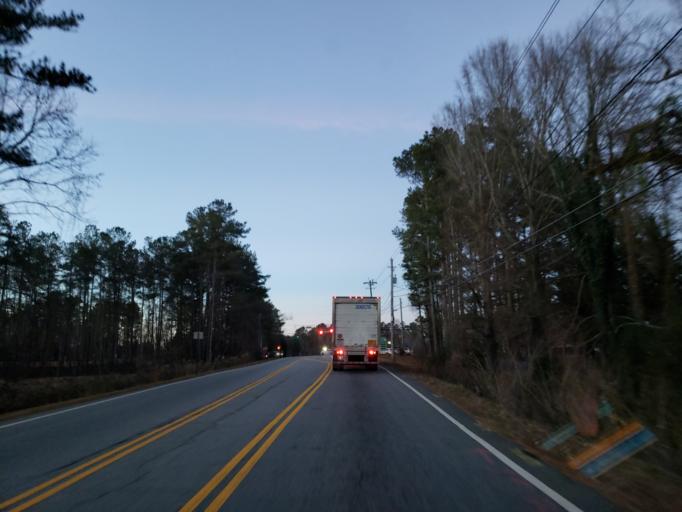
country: US
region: Georgia
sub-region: Cobb County
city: Acworth
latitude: 33.9696
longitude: -84.7104
